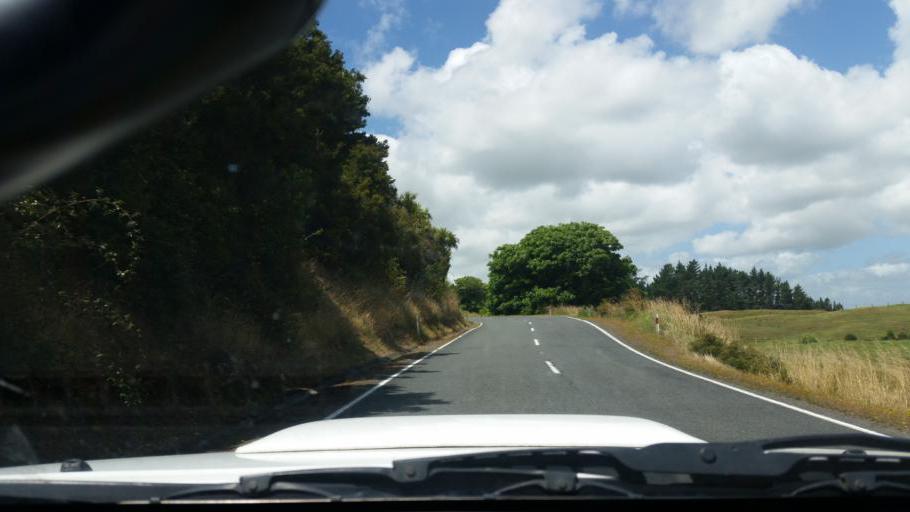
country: NZ
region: Northland
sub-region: Whangarei
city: Ruakaka
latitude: -36.0776
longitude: 174.2524
